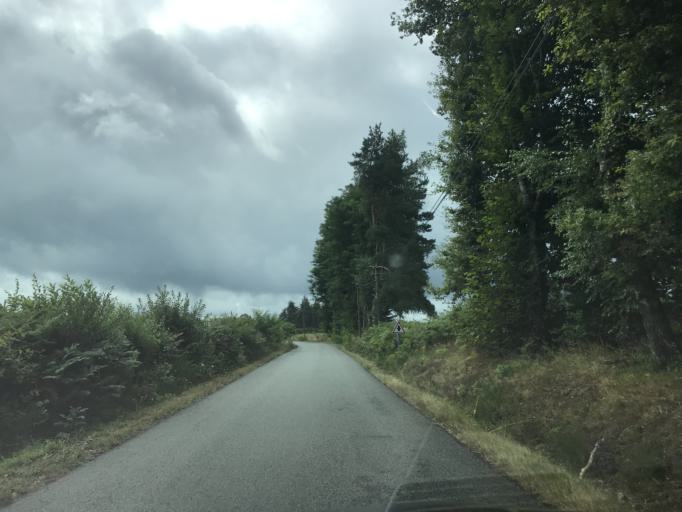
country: FR
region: Auvergne
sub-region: Departement du Cantal
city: Pleaux
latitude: 45.2473
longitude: 2.1960
